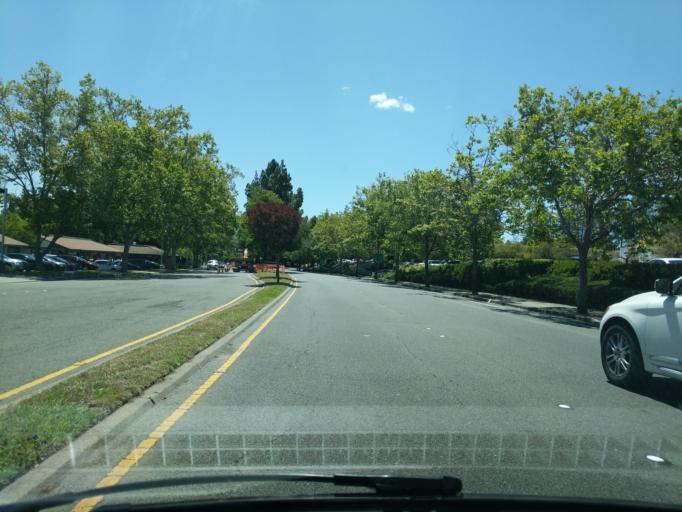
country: US
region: California
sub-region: Contra Costa County
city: Pleasant Hill
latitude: 37.9556
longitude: -122.0903
